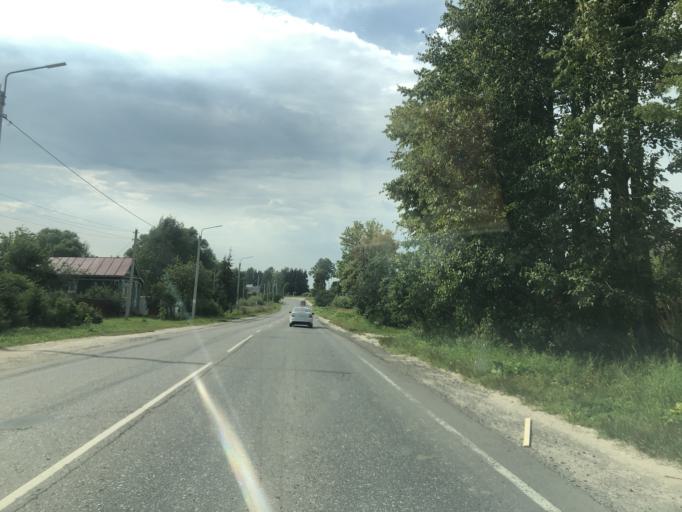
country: RU
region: Ivanovo
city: Shuya
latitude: 56.8577
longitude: 41.5051
